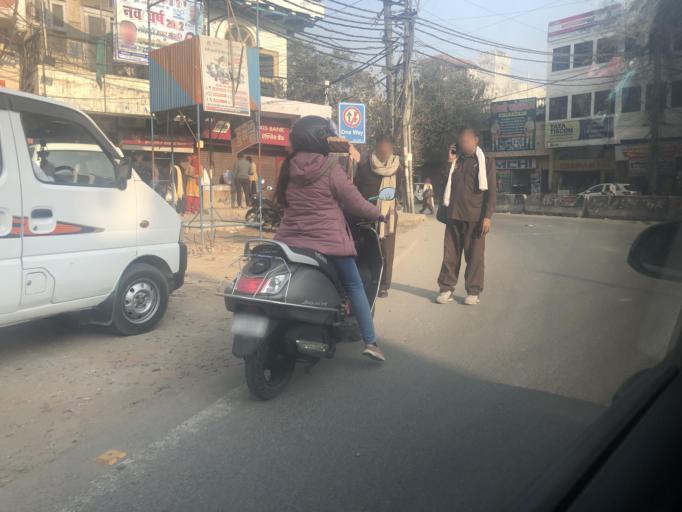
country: IN
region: Haryana
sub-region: Jhajjar
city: Bahadurgarh
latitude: 28.6136
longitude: 76.9799
